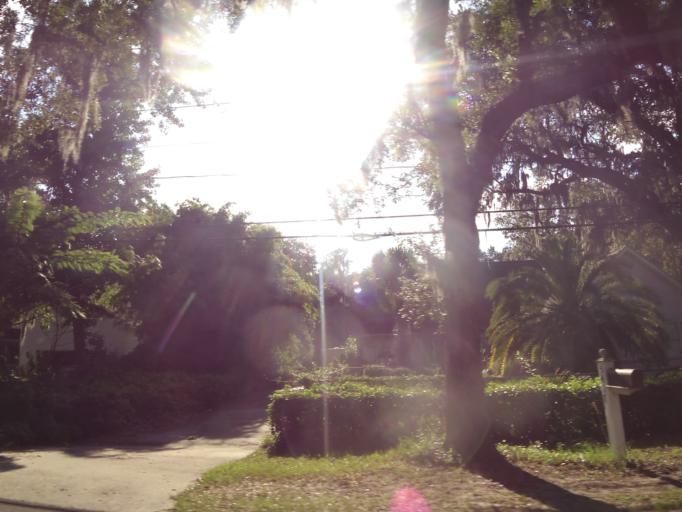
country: US
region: Georgia
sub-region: Glynn County
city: Saint Simon Mills
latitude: 31.2032
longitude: -81.3760
